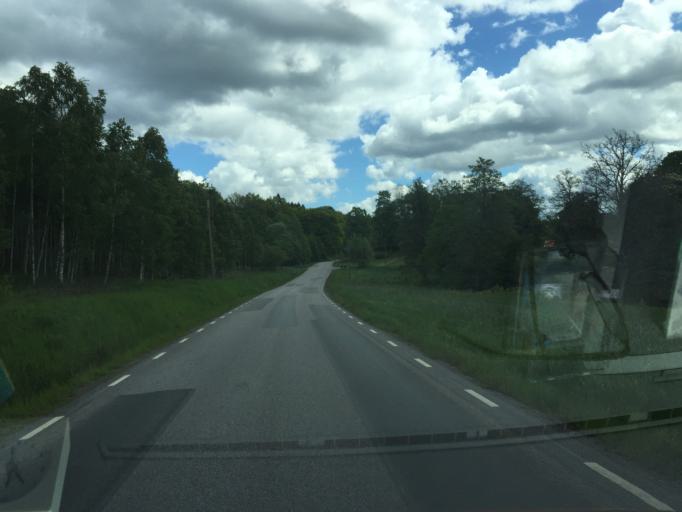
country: SE
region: OEstergoetland
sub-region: Finspangs Kommun
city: Finspang
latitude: 58.7086
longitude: 15.8579
